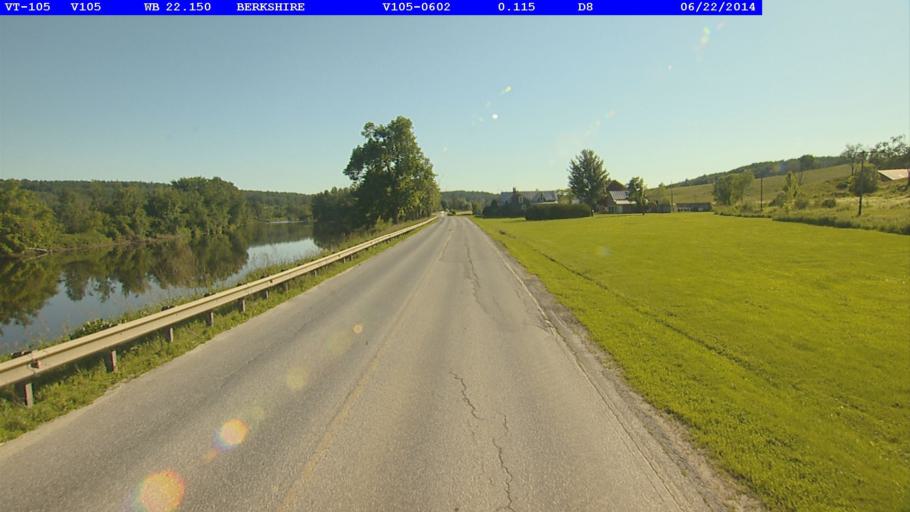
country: US
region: Vermont
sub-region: Franklin County
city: Enosburg Falls
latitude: 44.9277
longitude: -72.7249
